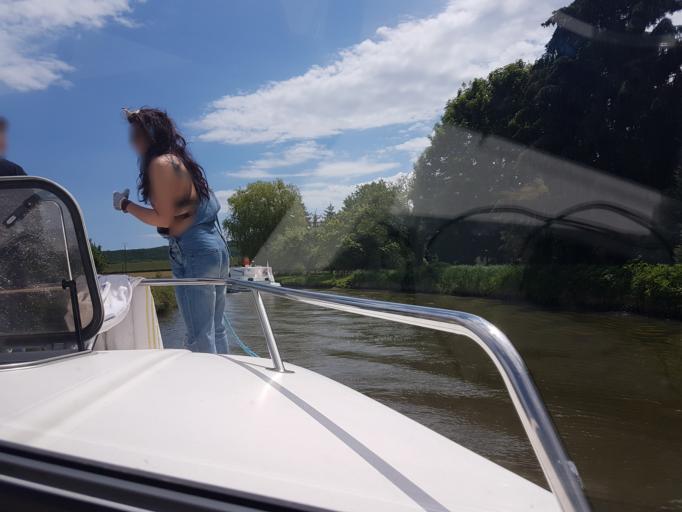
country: FR
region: Bourgogne
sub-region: Departement de la Nievre
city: Clamecy
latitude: 47.4907
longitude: 3.5122
